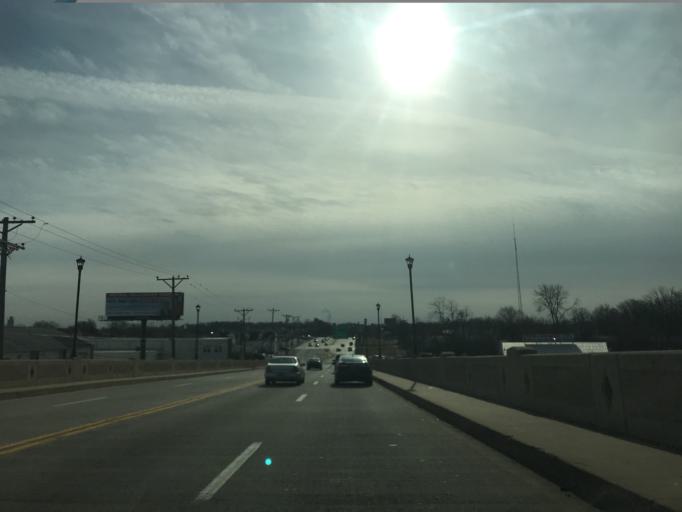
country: US
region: Delaware
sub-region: New Castle County
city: Wilmington
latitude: 39.7242
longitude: -75.5558
